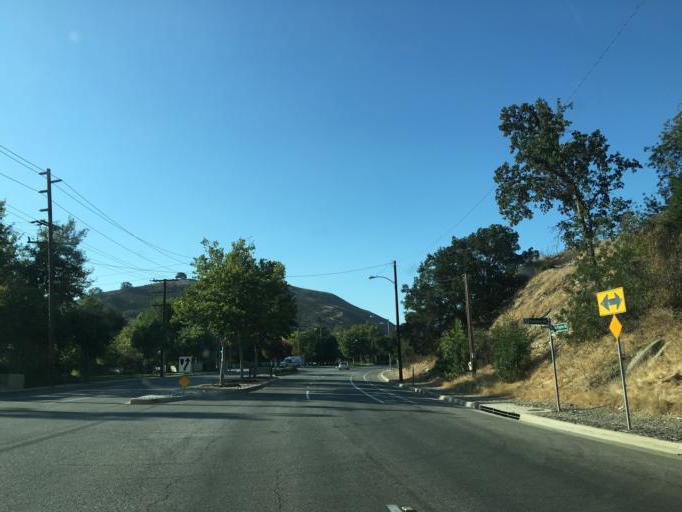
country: US
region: California
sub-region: Los Angeles County
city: Agoura
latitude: 34.1535
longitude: -118.6977
